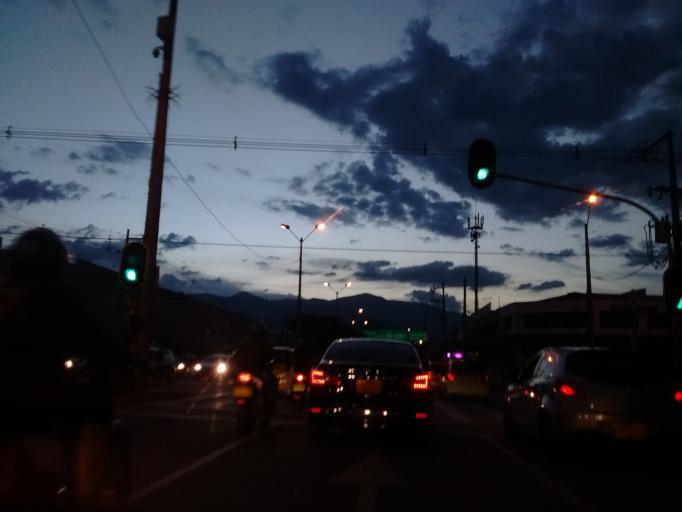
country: CO
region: Antioquia
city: Medellin
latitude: 6.2386
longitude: -75.5735
